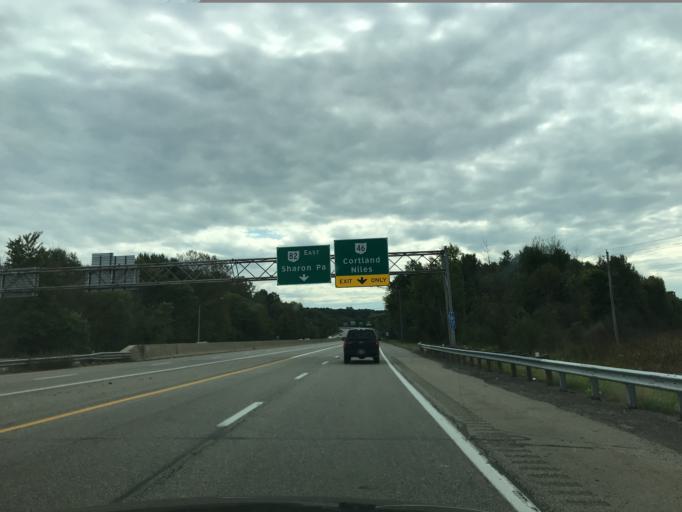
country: US
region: Ohio
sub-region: Trumbull County
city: Howland Center
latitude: 41.2339
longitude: -80.7514
